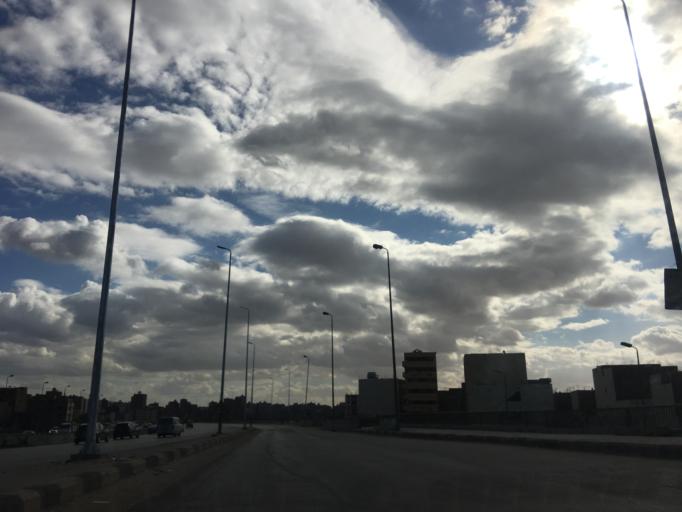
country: EG
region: Al Jizah
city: Al Jizah
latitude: 30.0285
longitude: 31.1631
